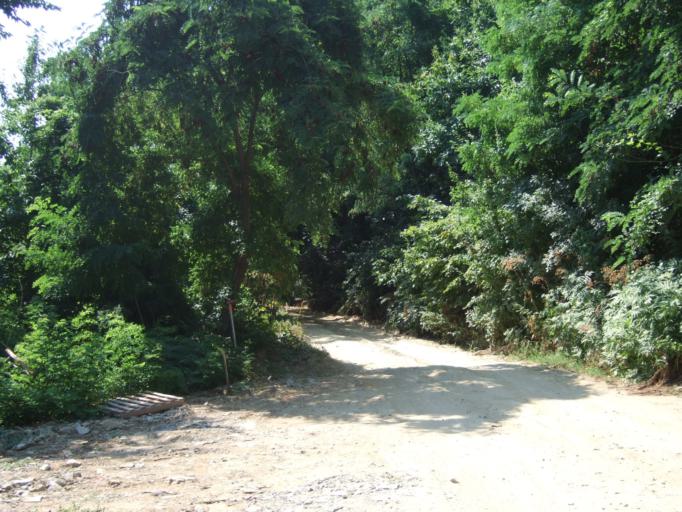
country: GR
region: Mount Athos
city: Karyes
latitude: 40.2691
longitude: 24.2302
